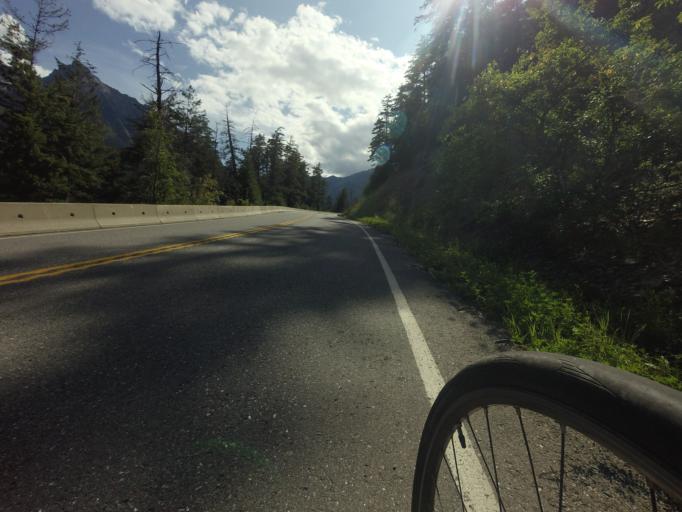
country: CA
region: British Columbia
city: Lillooet
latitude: 50.6514
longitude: -122.0164
